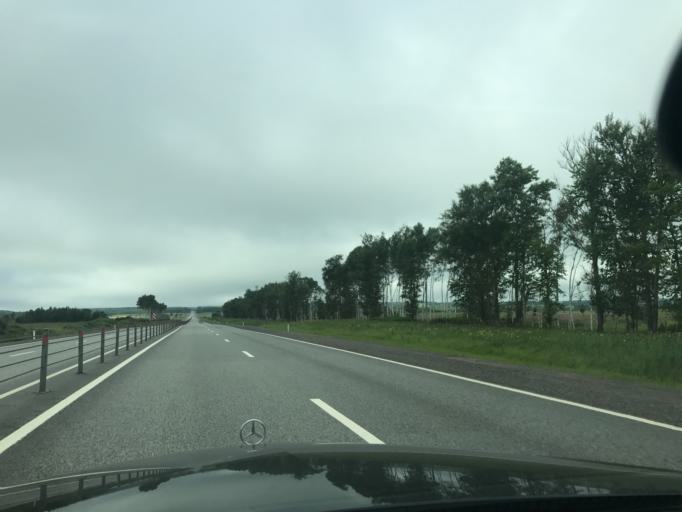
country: RU
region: Smolensk
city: Vyaz'ma
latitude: 55.3463
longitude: 34.6146
